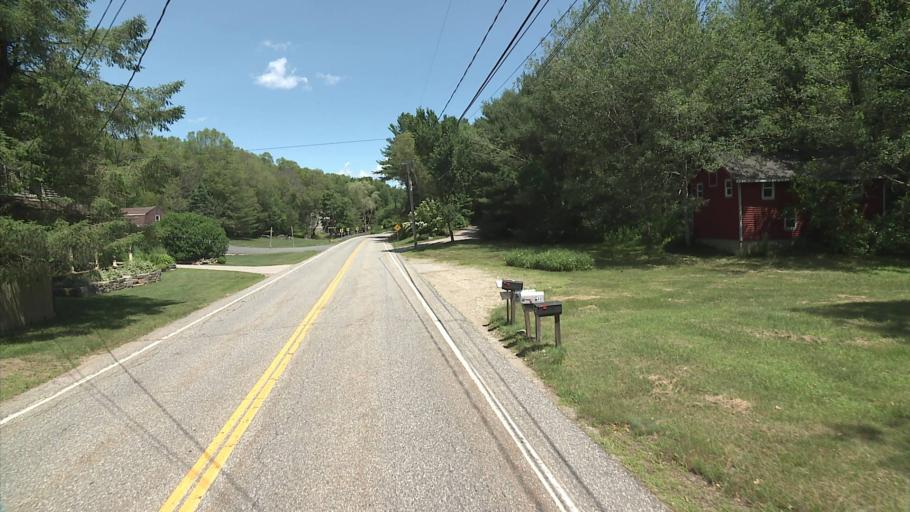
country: US
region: Connecticut
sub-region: New London County
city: Preston City
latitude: 41.5169
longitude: -71.8900
